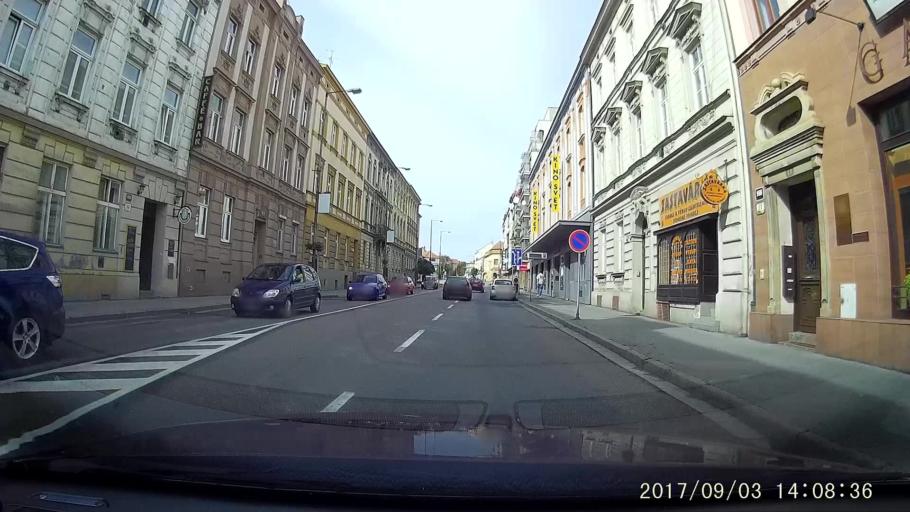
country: CZ
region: South Moravian
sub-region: Okres Znojmo
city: Znojmo
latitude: 48.8567
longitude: 16.0544
